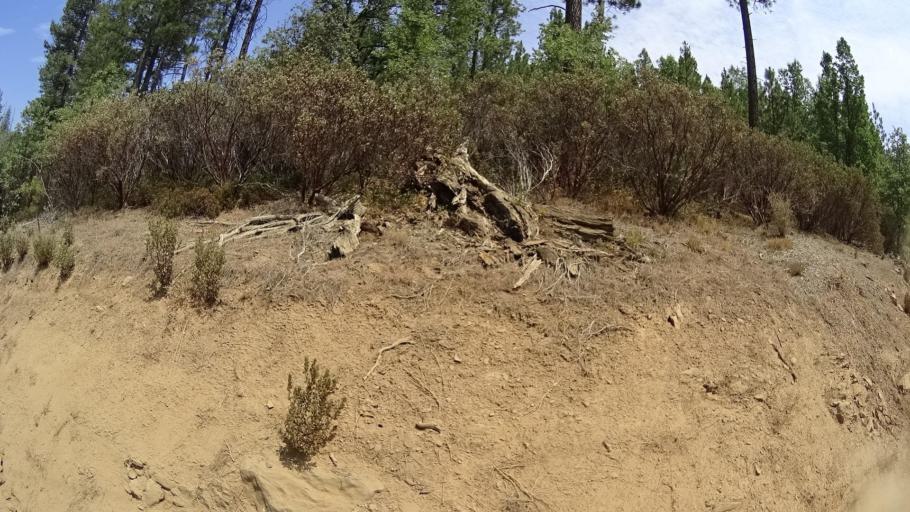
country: US
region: California
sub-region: Mariposa County
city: Midpines
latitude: 37.7457
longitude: -120.0676
